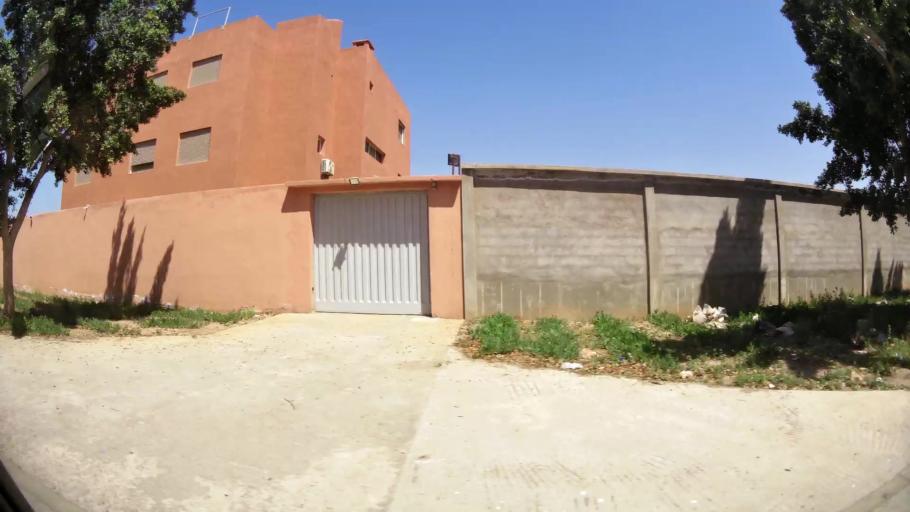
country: MA
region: Souss-Massa-Draa
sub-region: Inezgane-Ait Mellou
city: Inezgane
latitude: 30.3214
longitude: -9.4945
